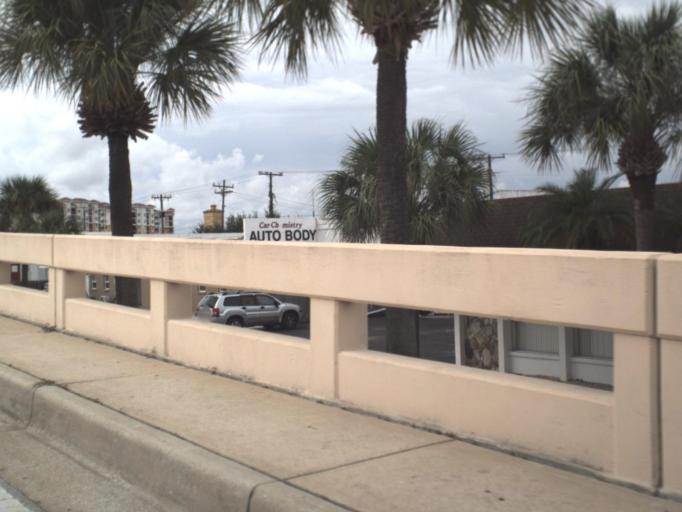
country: US
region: Florida
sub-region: Sarasota County
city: Venice
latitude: 27.0999
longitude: -82.4383
